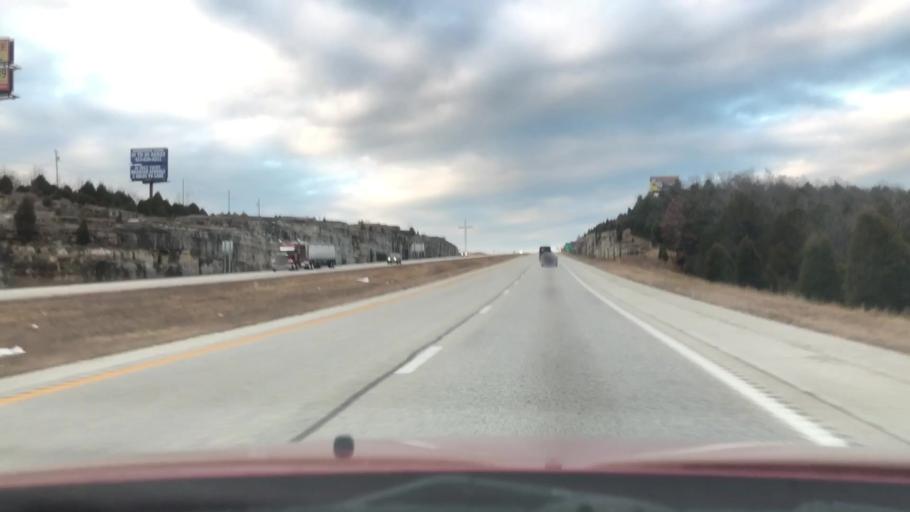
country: US
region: Missouri
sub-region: Taney County
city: Merriam Woods
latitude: 36.7393
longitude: -93.2215
